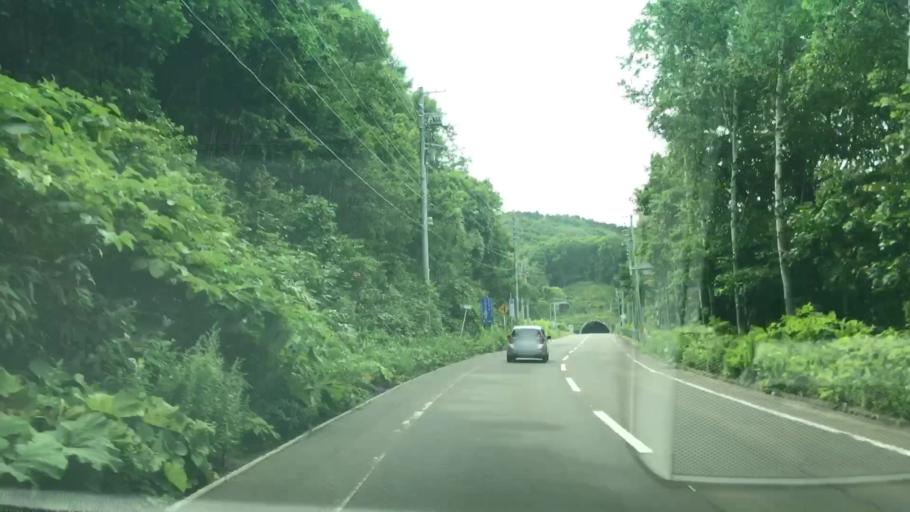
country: JP
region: Hokkaido
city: Yoichi
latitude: 43.1263
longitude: 140.8288
